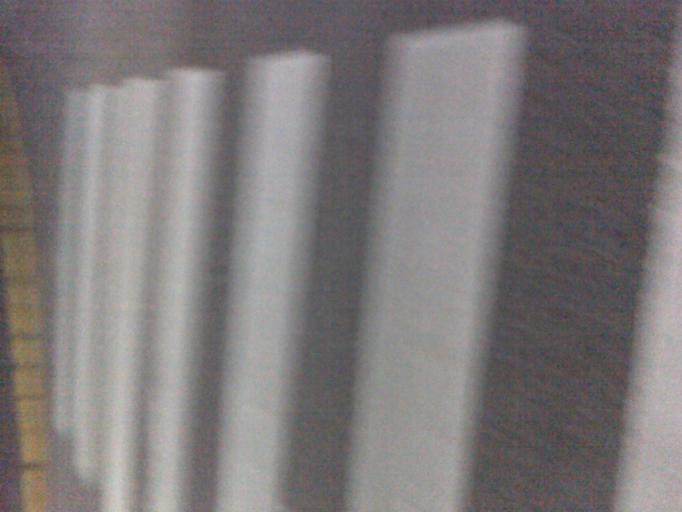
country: FR
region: Lower Normandy
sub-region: Departement de l'Orne
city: Saint-Denis-sur-Sarthon
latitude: 48.4570
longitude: -0.0482
